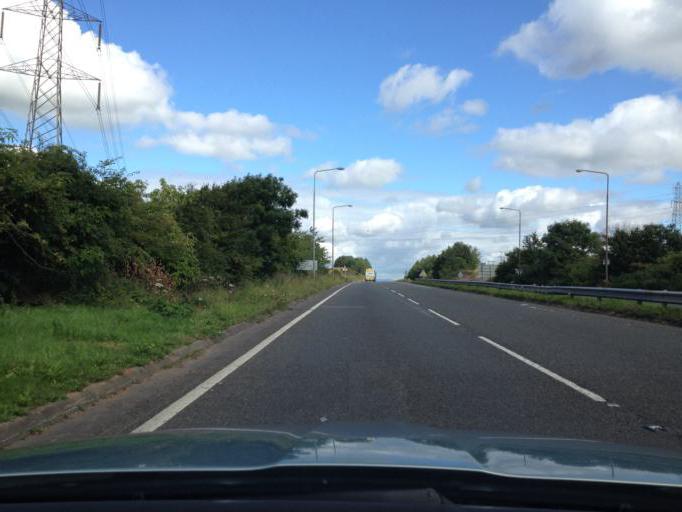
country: GB
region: Scotland
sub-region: West Lothian
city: Armadale
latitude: 55.9006
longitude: -3.6771
